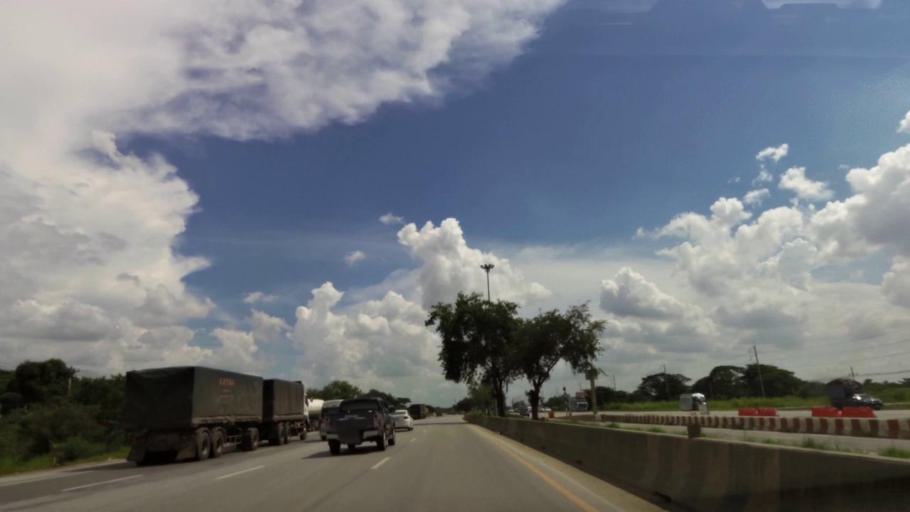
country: TH
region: Phra Nakhon Si Ayutthaya
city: Maha Rat
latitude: 14.5171
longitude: 100.5123
